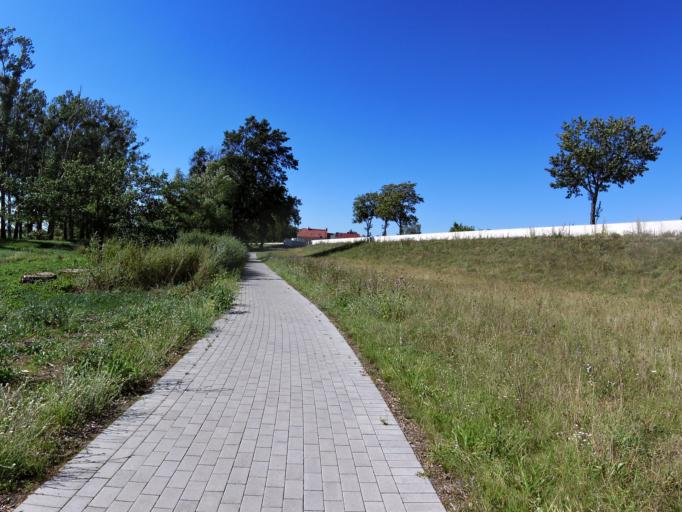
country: DE
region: Saxony-Anhalt
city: Elster
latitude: 51.8355
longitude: 12.7926
